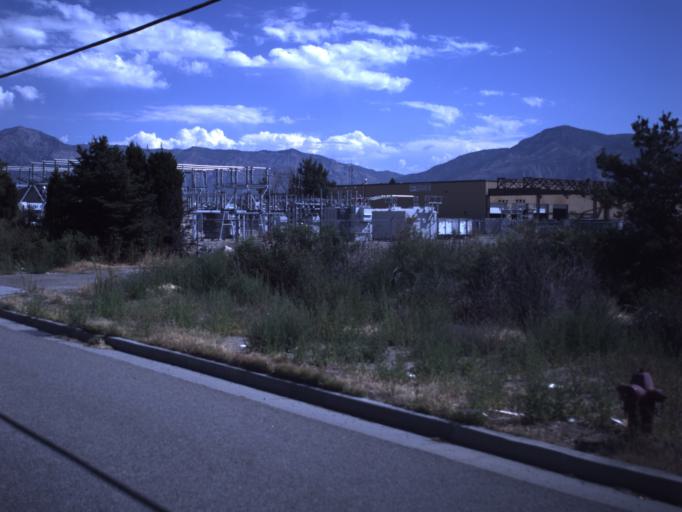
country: US
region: Utah
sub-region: Weber County
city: West Haven
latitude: 41.2177
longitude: -112.0256
